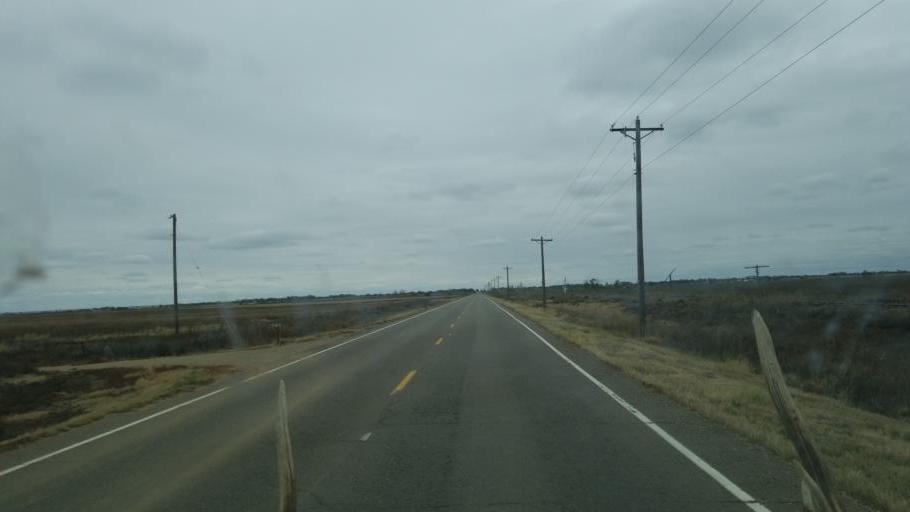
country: US
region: Colorado
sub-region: Crowley County
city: Ordway
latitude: 38.2267
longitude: -103.7019
